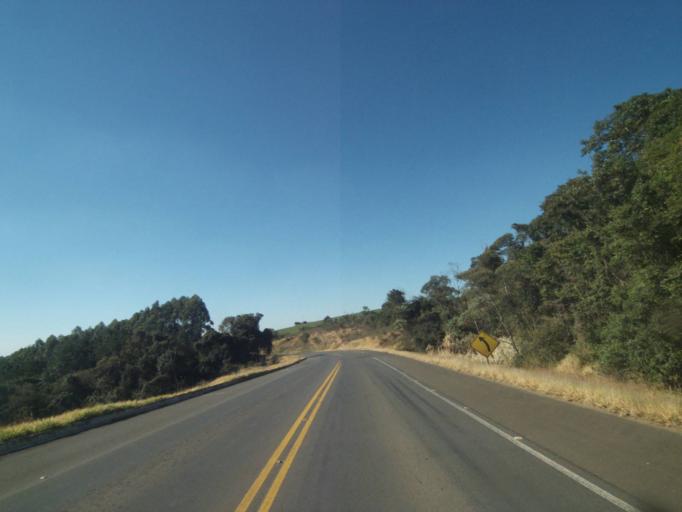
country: BR
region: Parana
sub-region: Tibagi
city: Tibagi
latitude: -24.7547
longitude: -50.4680
